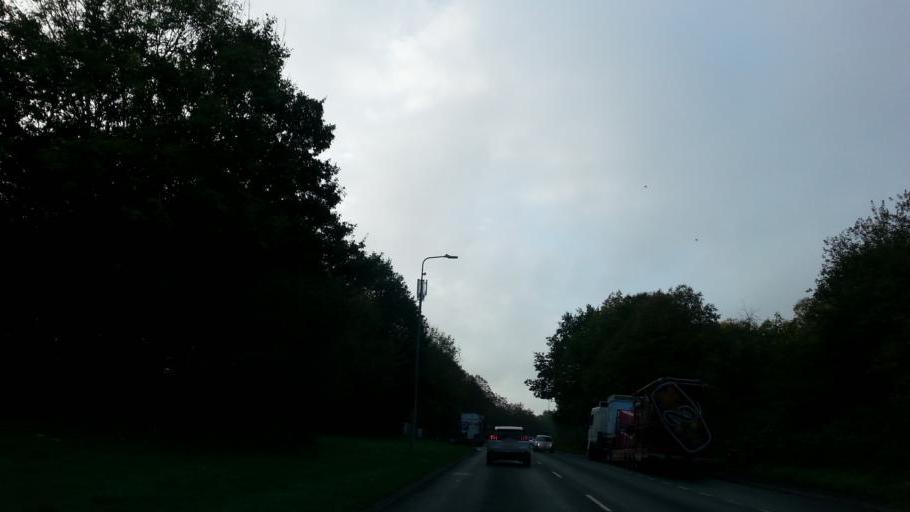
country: GB
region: England
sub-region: Worcestershire
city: Bromsgrove
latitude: 52.3385
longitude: -2.0477
